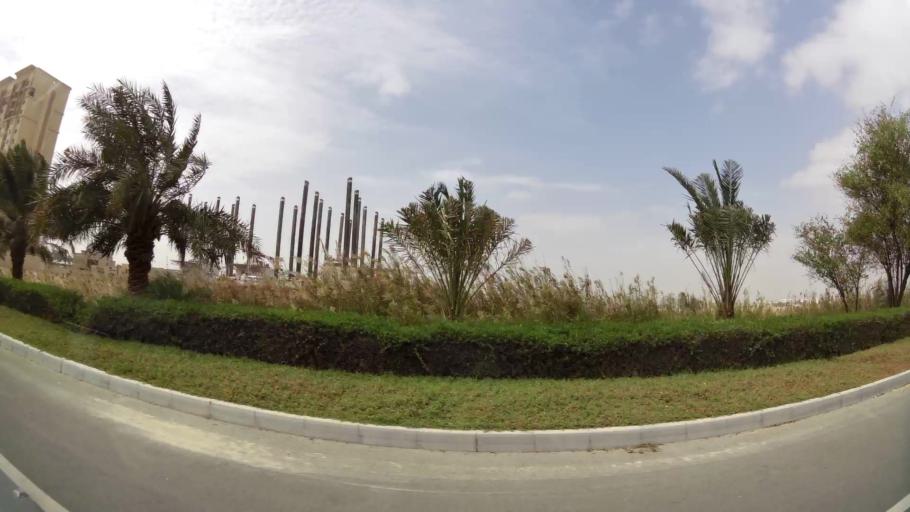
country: AE
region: Abu Dhabi
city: Abu Dhabi
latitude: 24.3868
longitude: 54.5228
